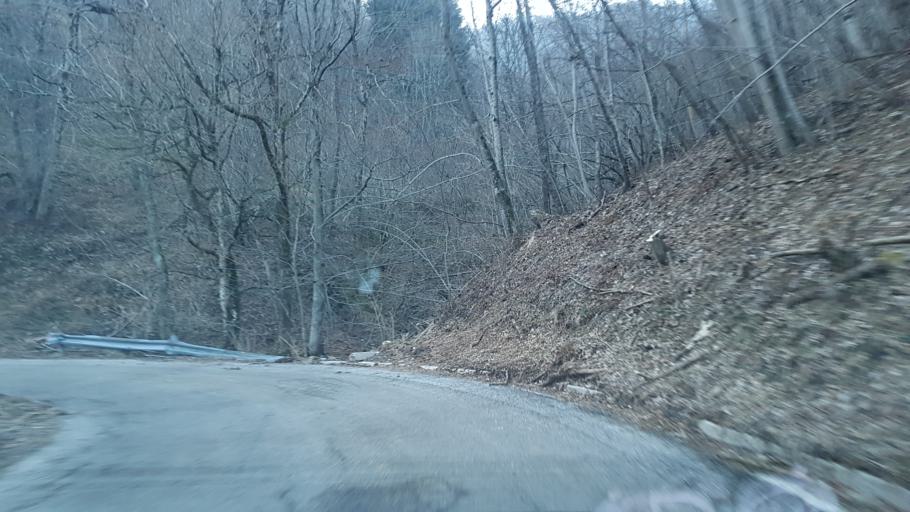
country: IT
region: Friuli Venezia Giulia
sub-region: Provincia di Udine
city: Taipana
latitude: 46.2126
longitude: 13.3794
